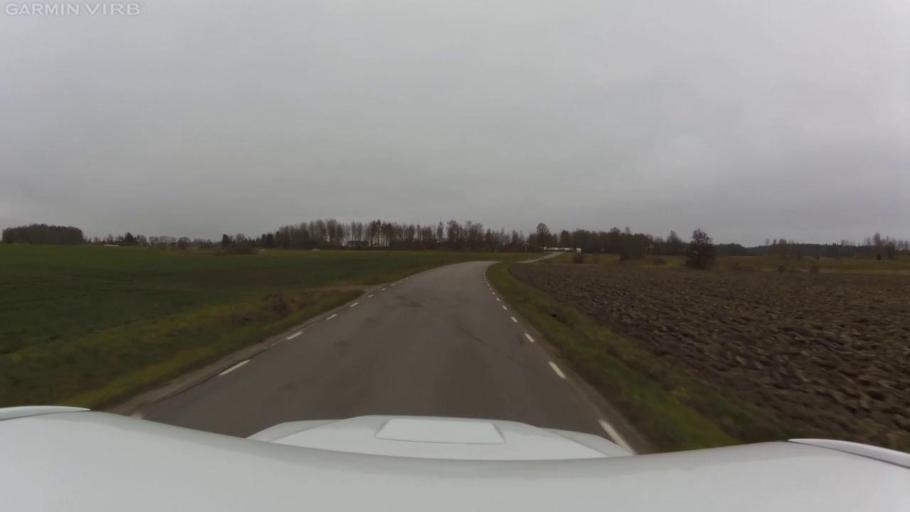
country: SE
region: OEstergoetland
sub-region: Linkopings Kommun
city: Vikingstad
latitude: 58.3167
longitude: 15.3766
